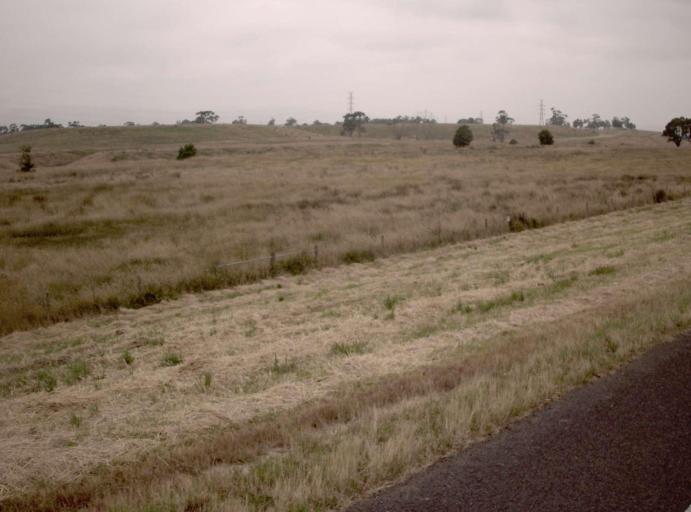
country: AU
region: Victoria
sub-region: Latrobe
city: Morwell
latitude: -38.2492
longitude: 146.3332
